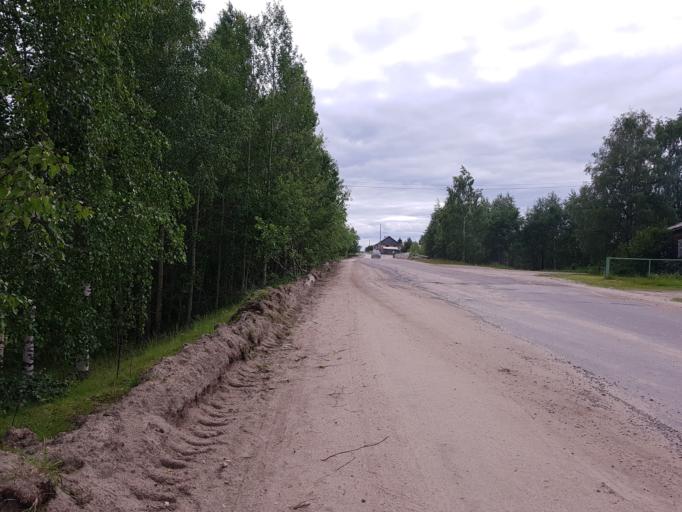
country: RU
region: Republic of Karelia
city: Kalevala
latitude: 65.1928
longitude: 31.1735
